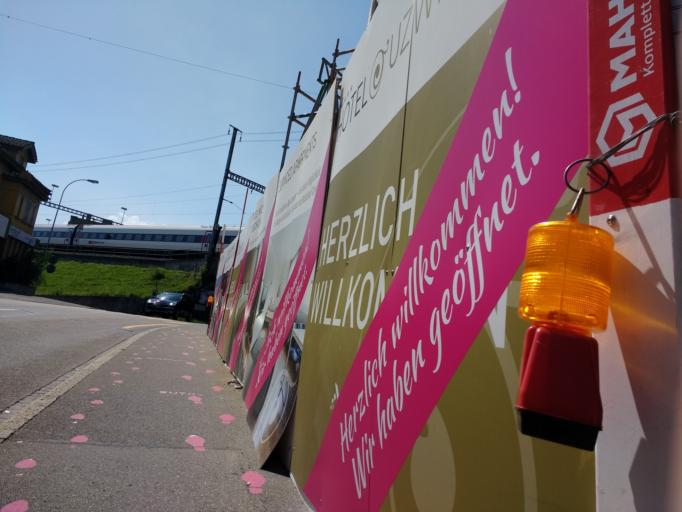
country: CH
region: Saint Gallen
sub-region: Wahlkreis Wil
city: Oberuzwil
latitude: 47.4363
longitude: 9.1319
